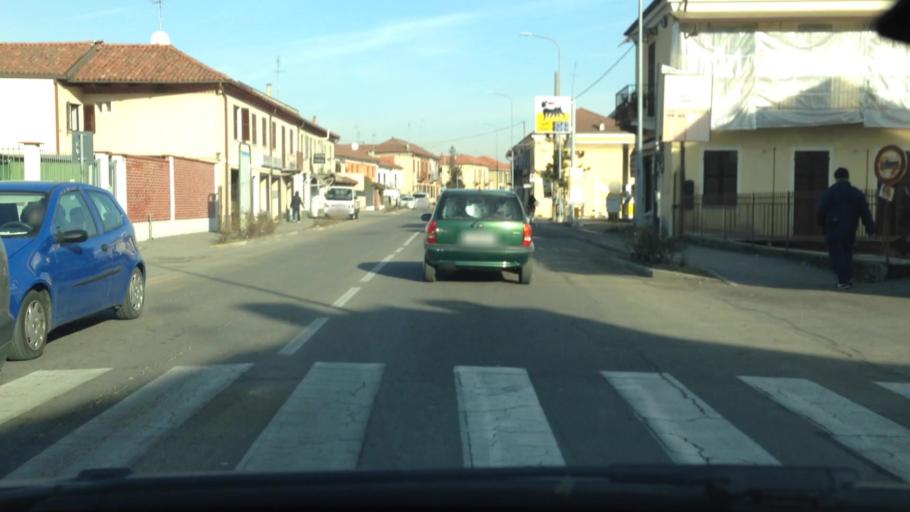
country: IT
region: Piedmont
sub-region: Provincia di Asti
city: Asti
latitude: 44.9113
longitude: 8.2197
